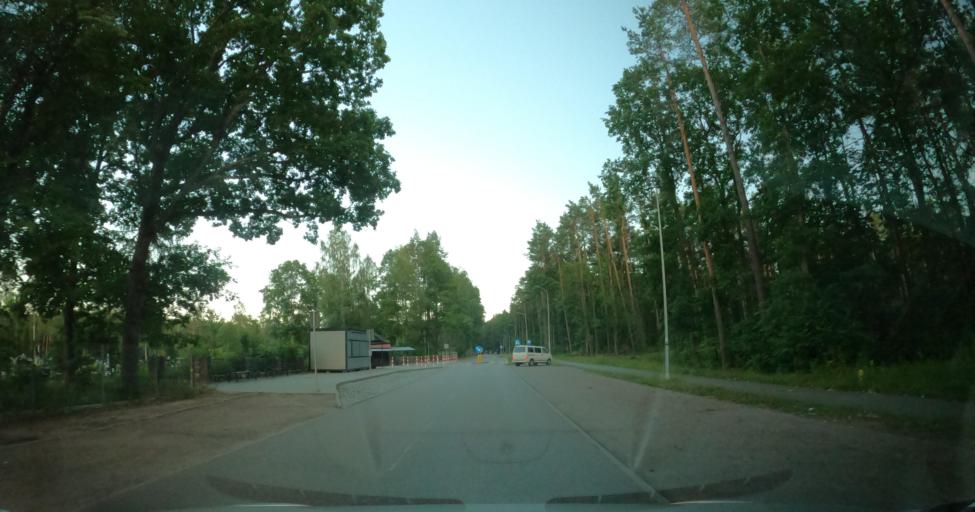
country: PL
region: Pomeranian Voivodeship
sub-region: Powiat leborski
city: Lebork
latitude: 54.5240
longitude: 17.7776
